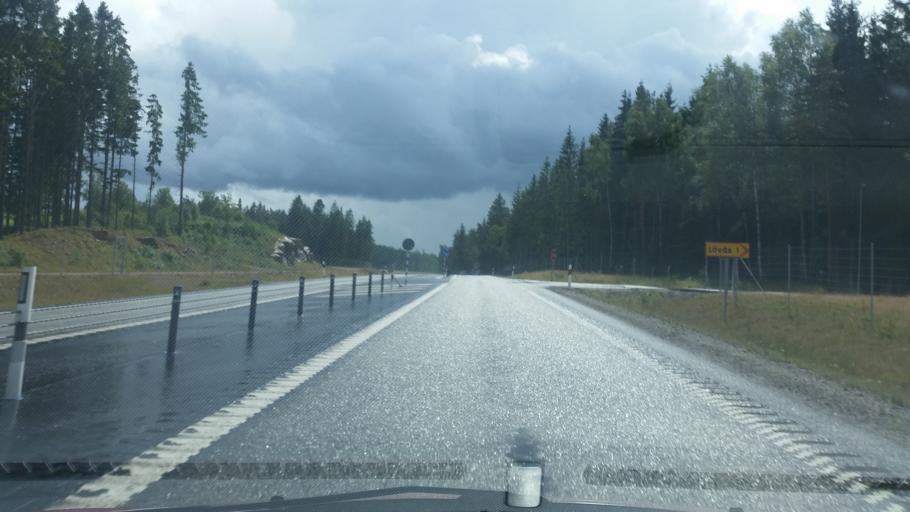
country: SE
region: Joenkoeping
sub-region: Gislaveds Kommun
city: Reftele
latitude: 57.2573
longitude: 13.6347
